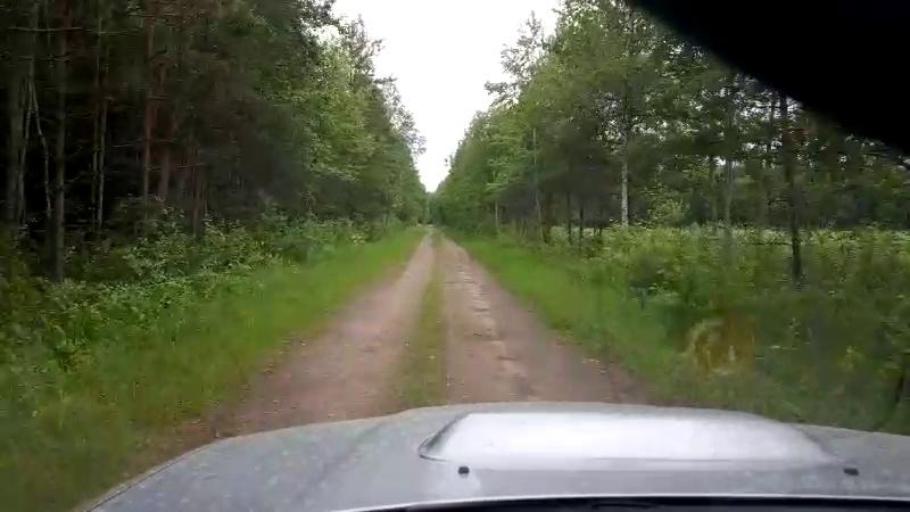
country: EE
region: Paernumaa
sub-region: Tootsi vald
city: Tootsi
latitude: 58.5513
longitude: 24.6842
